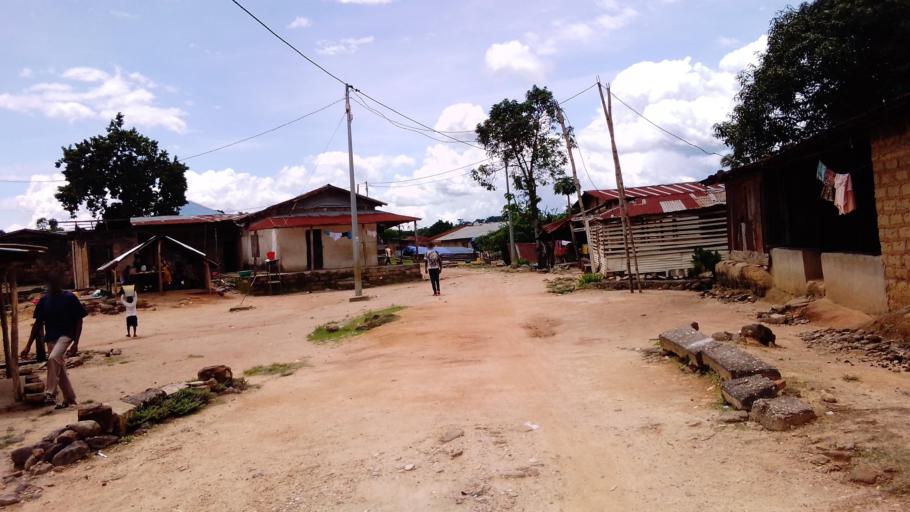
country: SL
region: Eastern Province
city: Koyima
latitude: 8.7013
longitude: -11.0094
